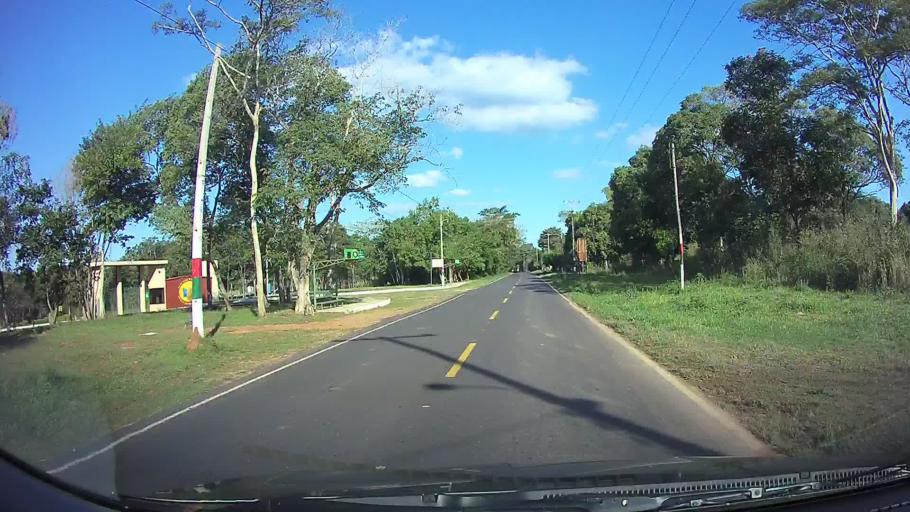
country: PY
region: Central
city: Aregua
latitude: -25.2899
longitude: -57.3946
